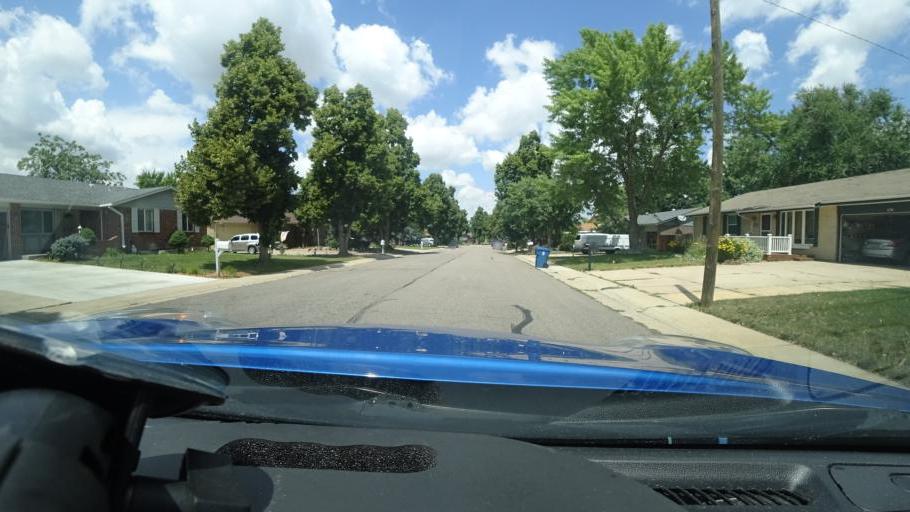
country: US
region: Colorado
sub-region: Adams County
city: Aurora
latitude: 39.7059
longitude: -104.8378
